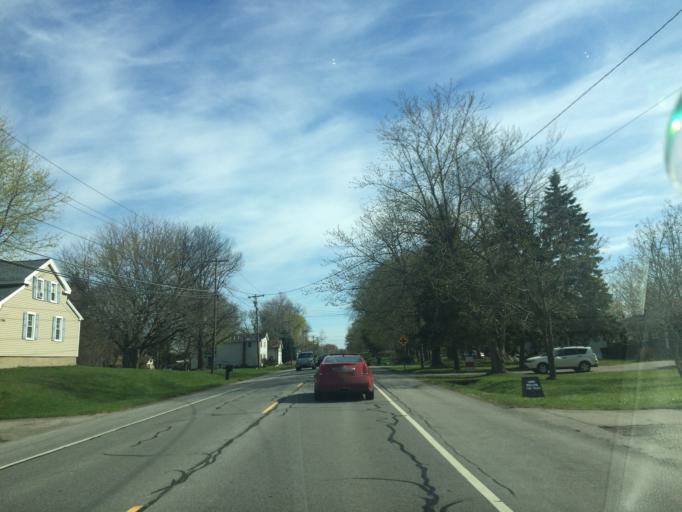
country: US
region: New York
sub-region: Monroe County
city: Webster
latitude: 43.1694
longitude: -77.4311
